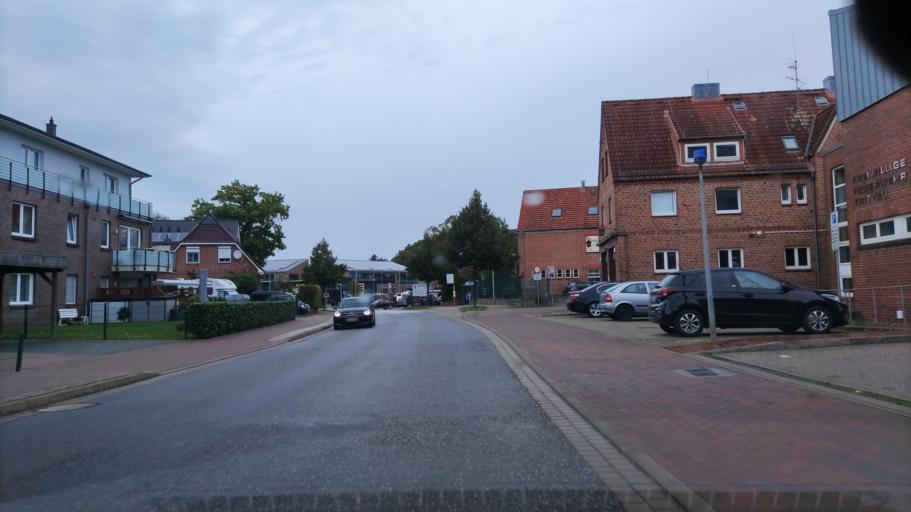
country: DE
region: Schleswig-Holstein
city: Trittau
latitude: 53.6084
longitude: 10.4068
